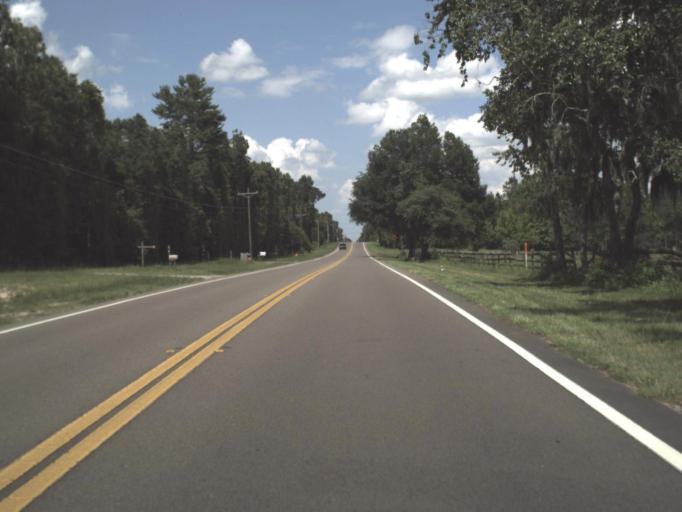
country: US
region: Florida
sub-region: Clay County
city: Keystone Heights
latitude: 29.7189
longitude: -82.0031
